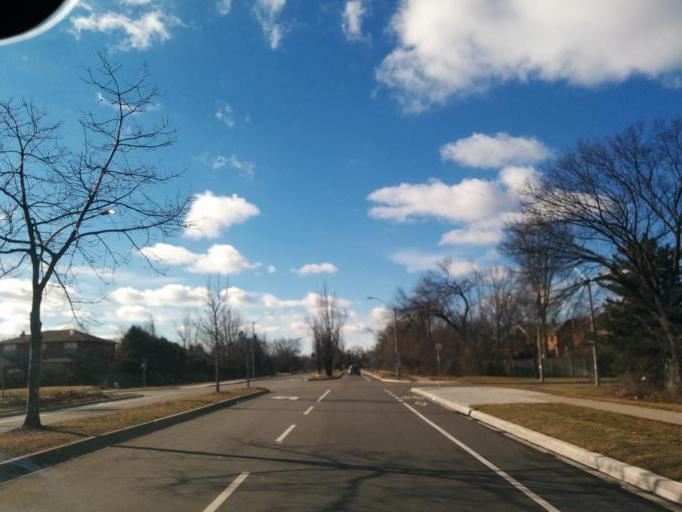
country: CA
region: Ontario
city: Mississauga
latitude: 43.5622
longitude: -79.6286
